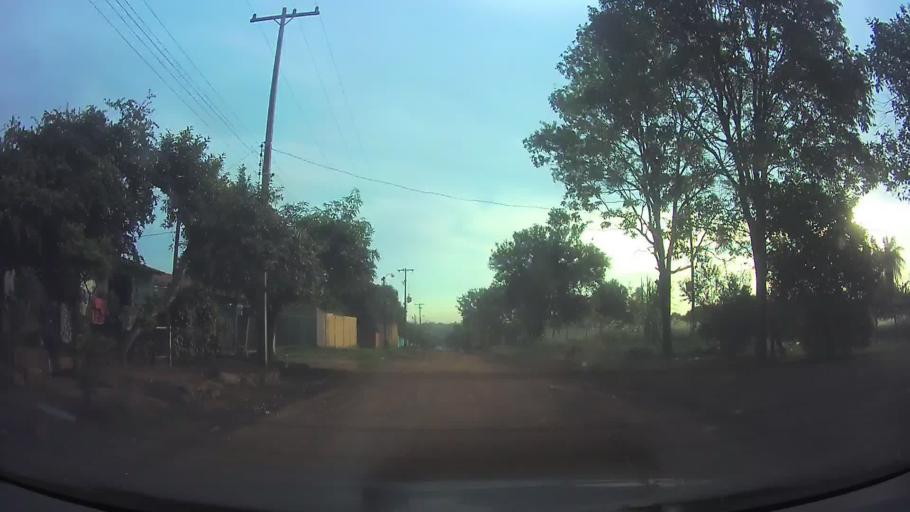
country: PY
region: Central
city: Limpio
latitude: -25.2446
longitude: -57.4550
